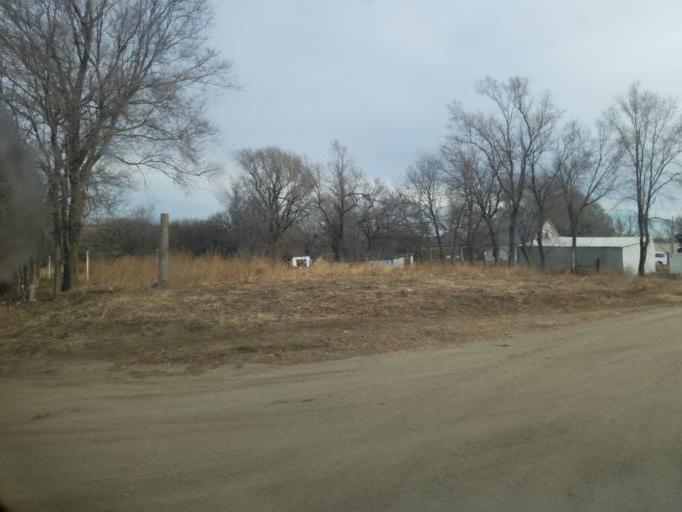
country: US
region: Nebraska
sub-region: Knox County
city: Center
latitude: 42.6161
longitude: -97.8378
